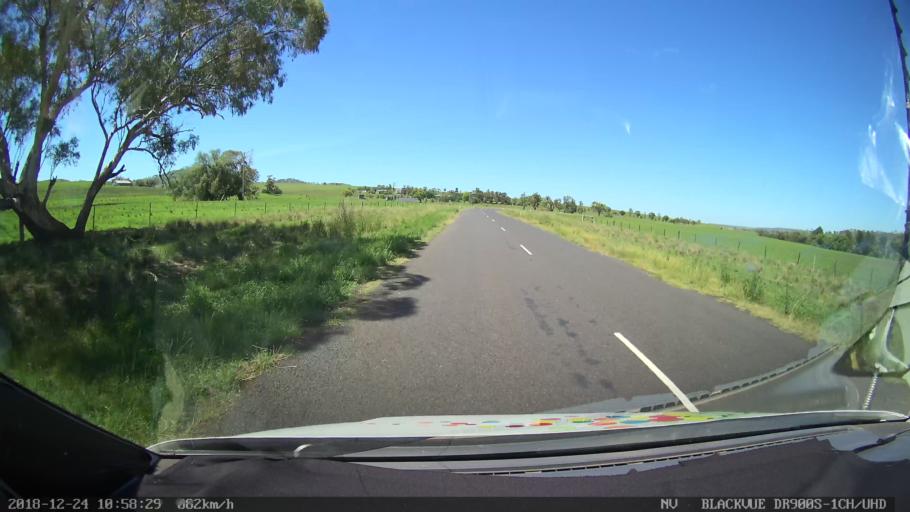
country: AU
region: New South Wales
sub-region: Upper Hunter Shire
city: Merriwa
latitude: -32.0480
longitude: 150.4062
